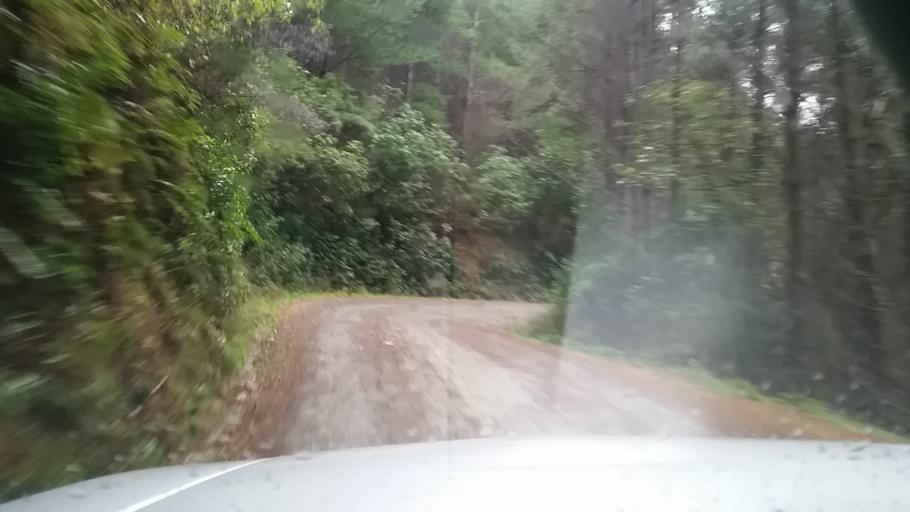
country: NZ
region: Marlborough
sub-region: Marlborough District
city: Picton
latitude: -41.1372
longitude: 174.0553
